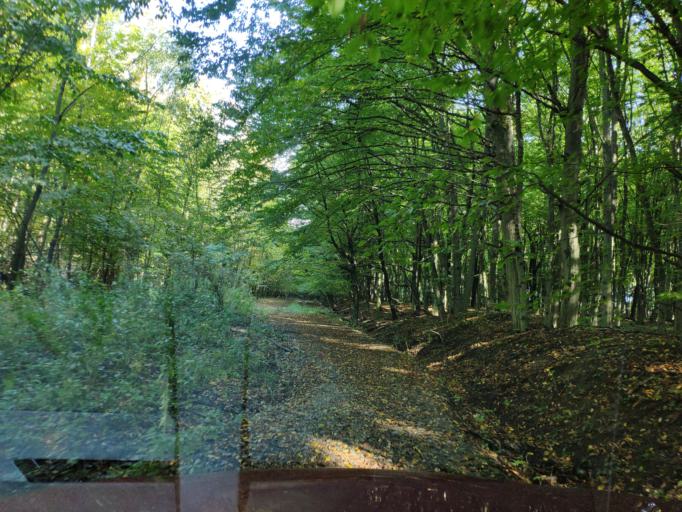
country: SK
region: Presovsky
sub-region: Okres Presov
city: Presov
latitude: 48.9334
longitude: 21.2748
